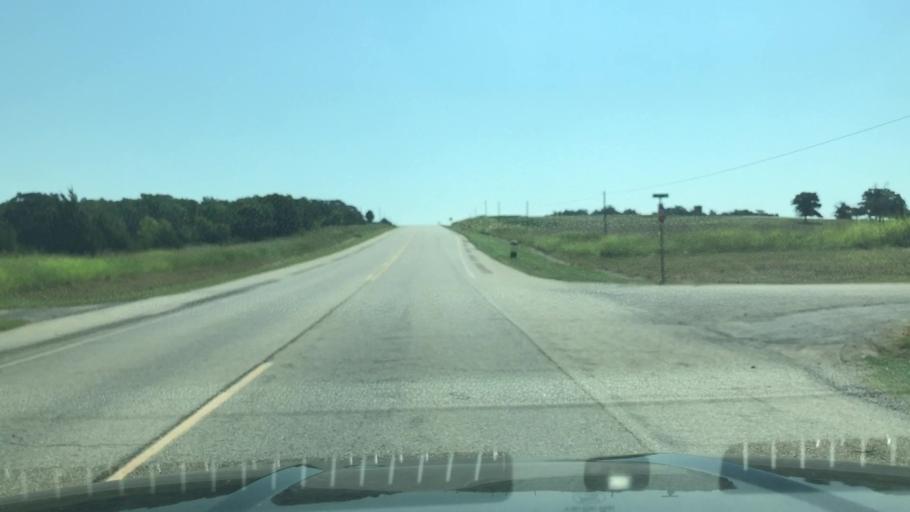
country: US
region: Oklahoma
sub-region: Creek County
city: Mannford
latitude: 36.0031
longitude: -96.4225
